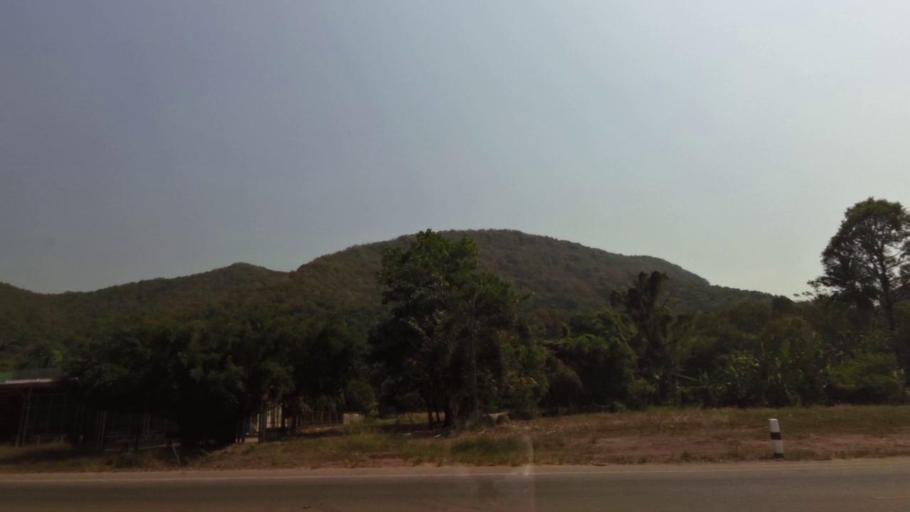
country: TH
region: Chanthaburi
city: Tha Mai
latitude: 12.5677
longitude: 101.9154
